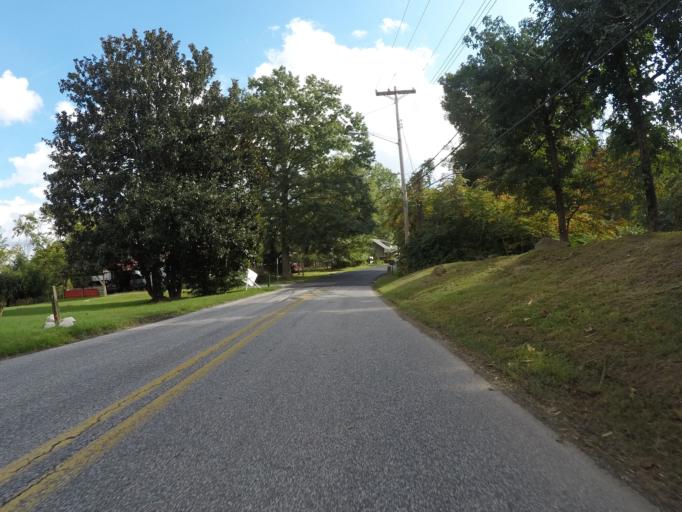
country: US
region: West Virginia
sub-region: Cabell County
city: Huntington
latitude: 38.3958
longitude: -82.4333
